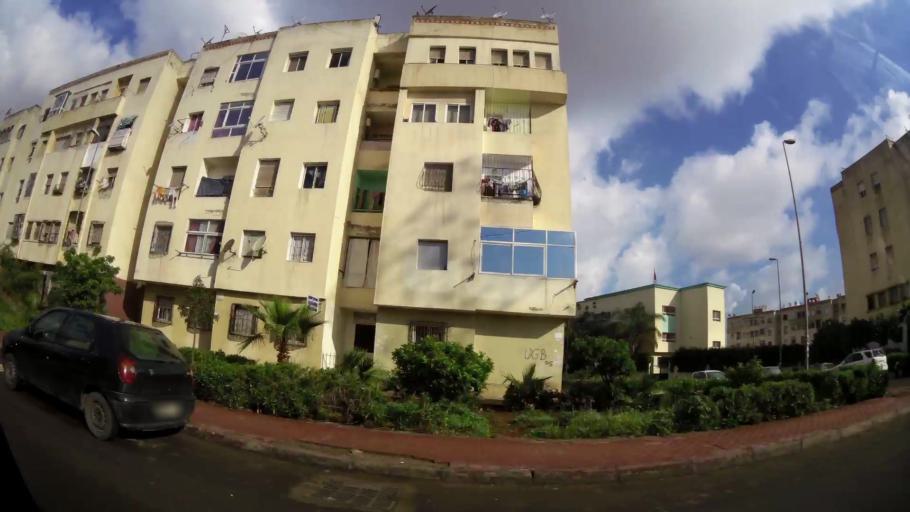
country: MA
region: Grand Casablanca
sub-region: Mediouna
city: Tit Mellil
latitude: 33.5937
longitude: -7.5324
